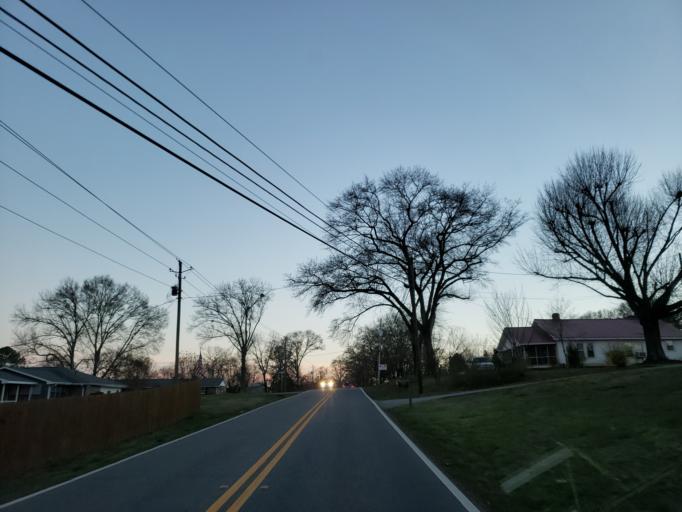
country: US
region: Georgia
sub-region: Bartow County
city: Cartersville
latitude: 34.1967
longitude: -84.8196
